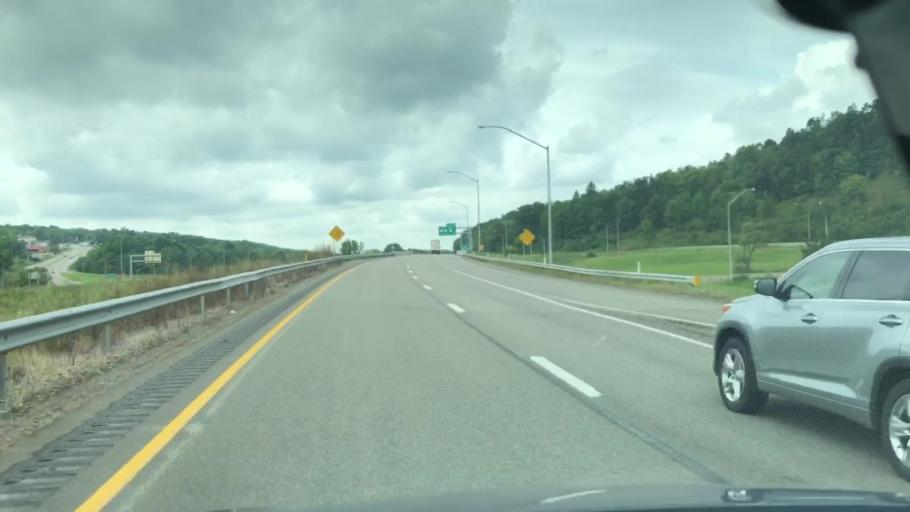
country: US
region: Pennsylvania
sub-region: Crawford County
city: Meadville
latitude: 41.6211
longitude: -80.1787
